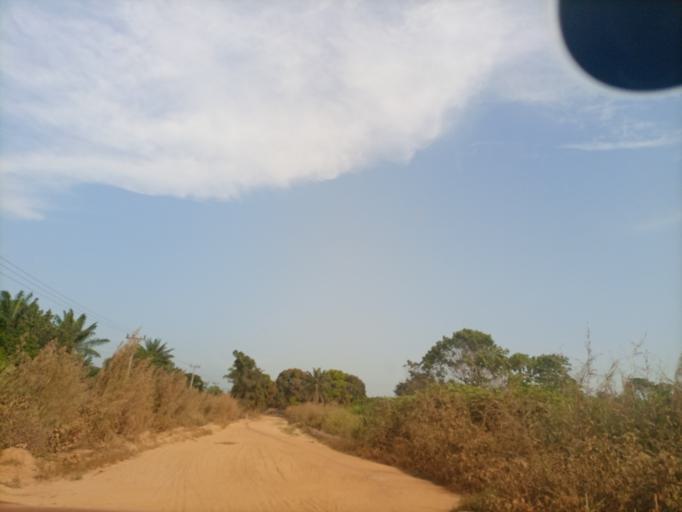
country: NG
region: Enugu
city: Obolo-Eke (1)
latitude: 6.8092
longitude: 7.5512
